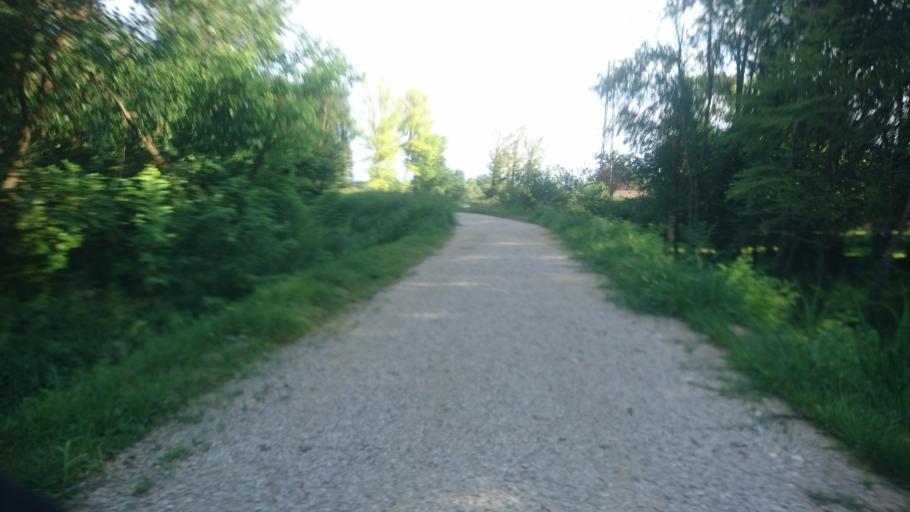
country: IT
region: Veneto
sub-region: Provincia di Padova
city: Villaguattera
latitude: 45.4348
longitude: 11.8291
